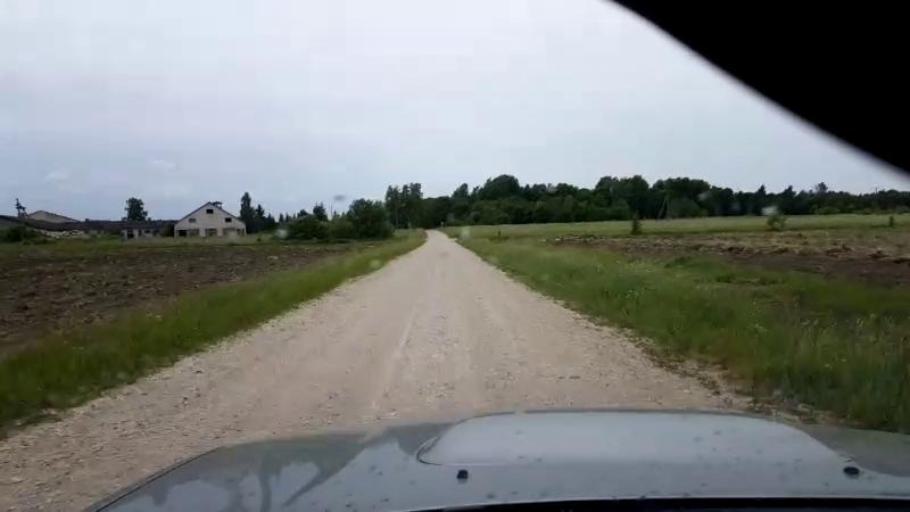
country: EE
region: Paernumaa
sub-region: Halinga vald
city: Parnu-Jaagupi
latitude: 58.5326
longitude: 24.5898
